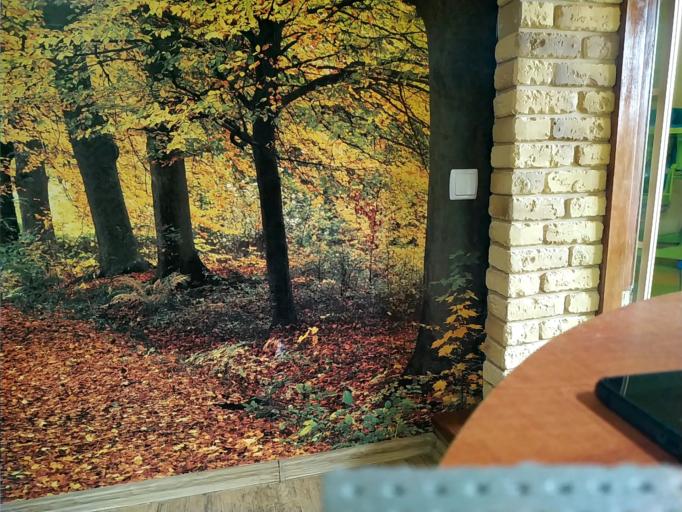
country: RU
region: Tverskaya
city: Likhoslavl'
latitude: 56.9852
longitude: 35.3211
